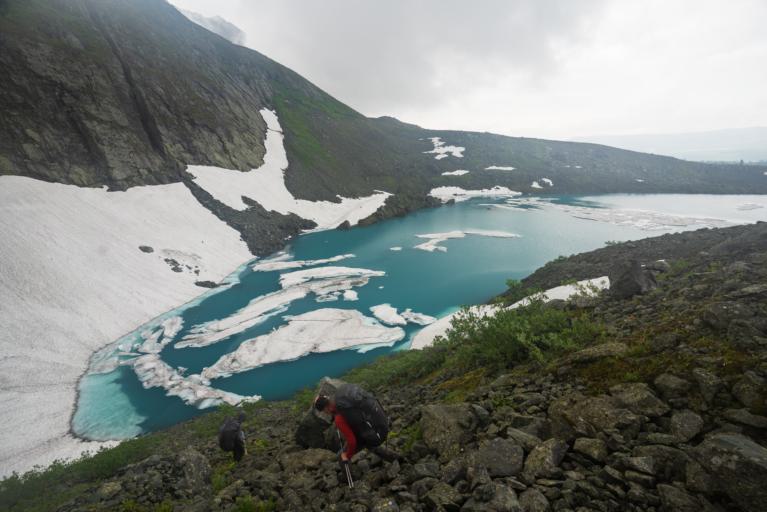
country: RU
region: Komi Republic
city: Synya
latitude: 64.7842
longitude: 58.9036
